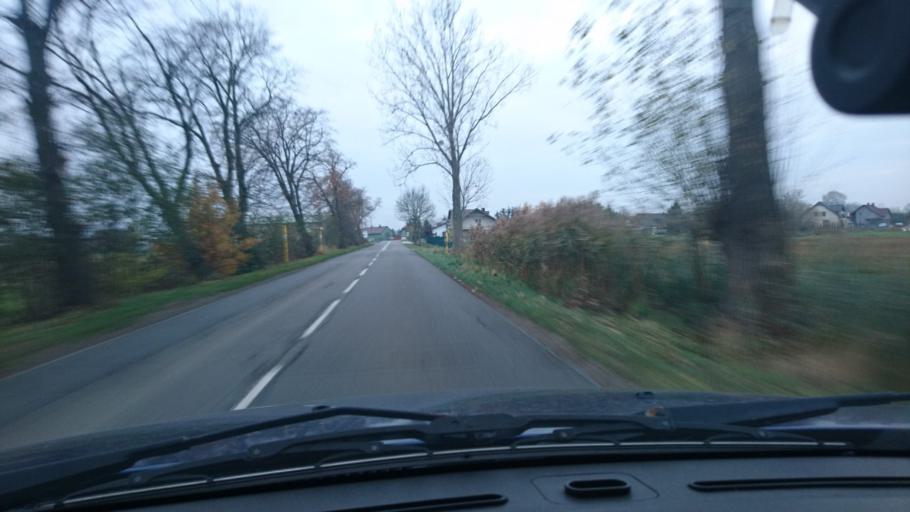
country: PL
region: Greater Poland Voivodeship
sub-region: Powiat ostrowski
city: Odolanow
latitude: 51.5443
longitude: 17.6553
